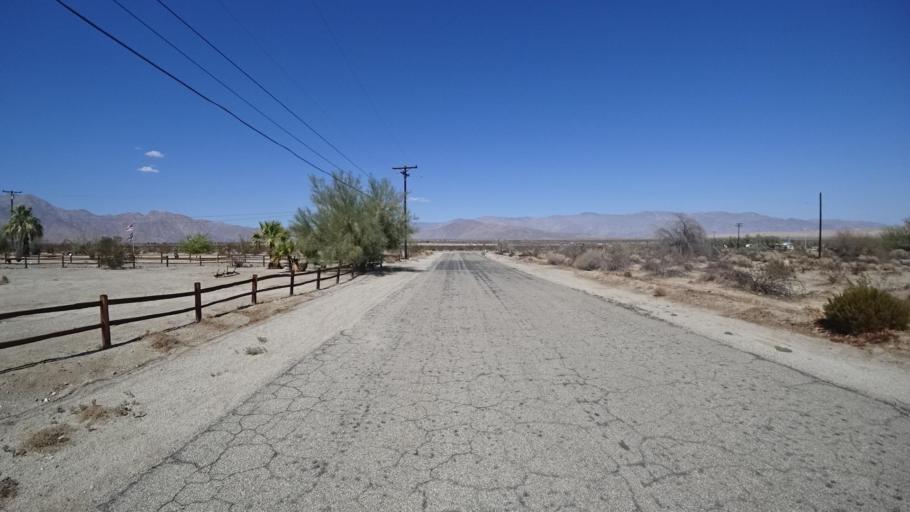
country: US
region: California
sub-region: San Diego County
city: Borrego Springs
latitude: 33.2101
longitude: -116.3355
